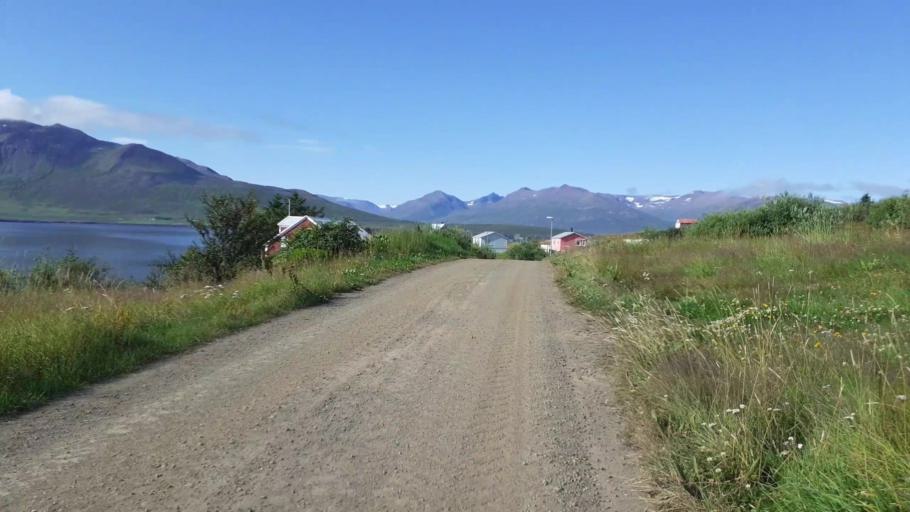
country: IS
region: Northeast
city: Dalvik
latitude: 65.9799
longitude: -18.3604
